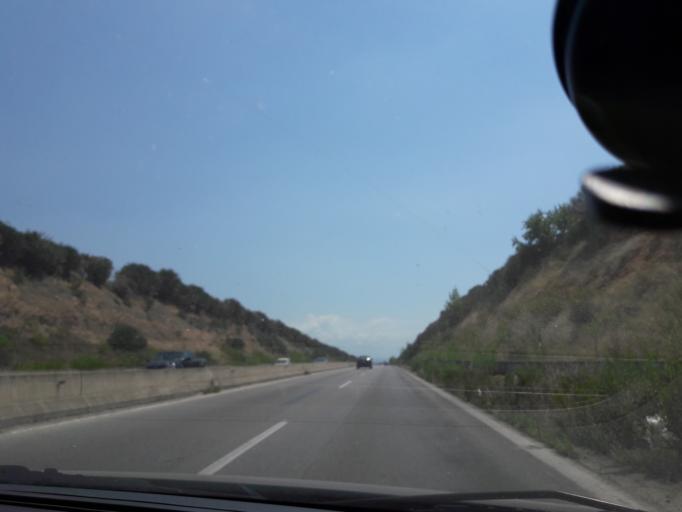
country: GR
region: Central Macedonia
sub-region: Nomos Chalkidikis
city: Nea Triglia
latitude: 40.2980
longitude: 23.1375
